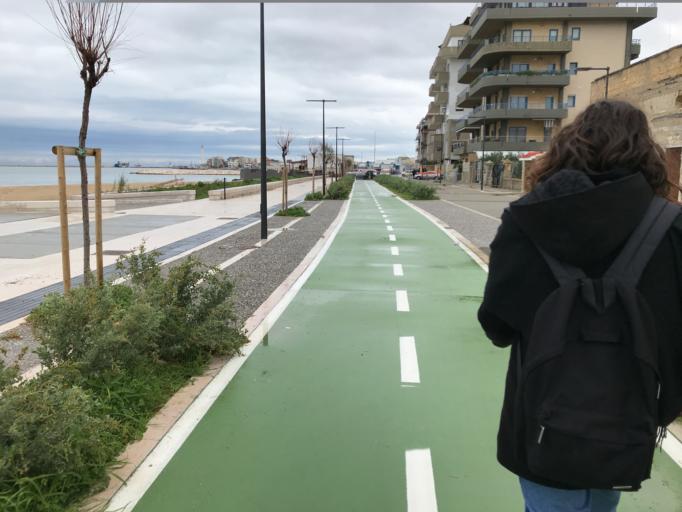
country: IT
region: Apulia
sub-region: Provincia di Bari
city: San Paolo
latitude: 41.1376
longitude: 16.8243
